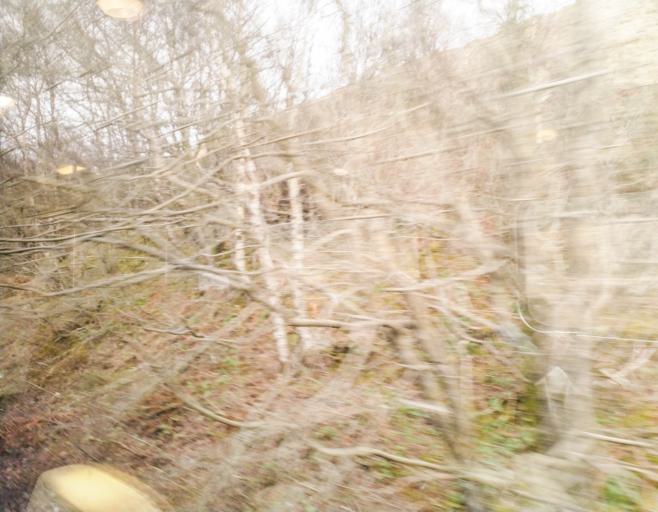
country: GB
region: Scotland
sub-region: Argyll and Bute
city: Garelochhead
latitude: 56.4690
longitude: -4.7169
